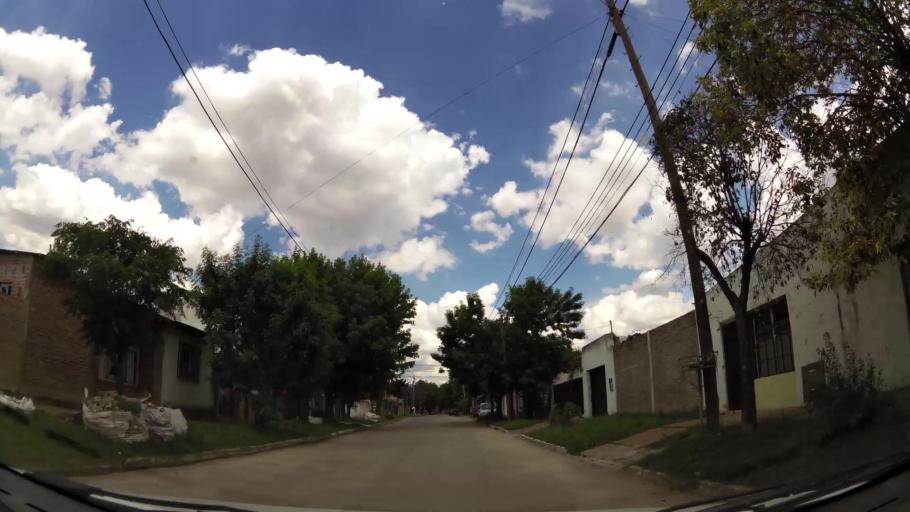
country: AR
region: Buenos Aires
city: Ituzaingo
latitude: -34.6472
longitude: -58.6822
